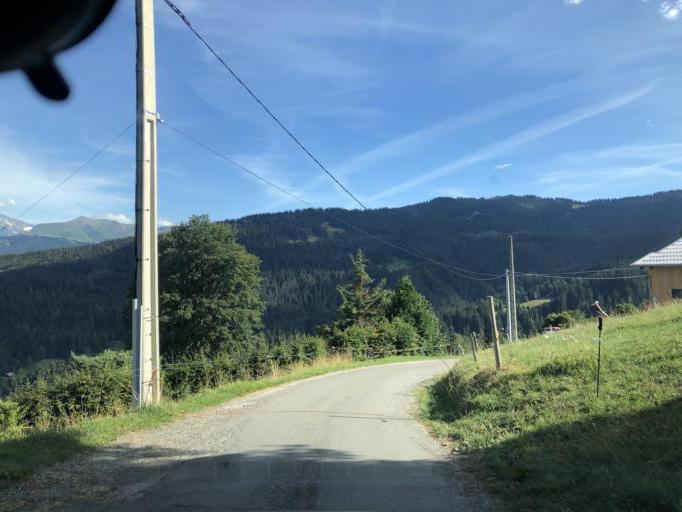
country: FR
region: Rhone-Alpes
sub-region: Departement de la Haute-Savoie
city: Cordon
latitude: 45.9116
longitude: 6.5893
